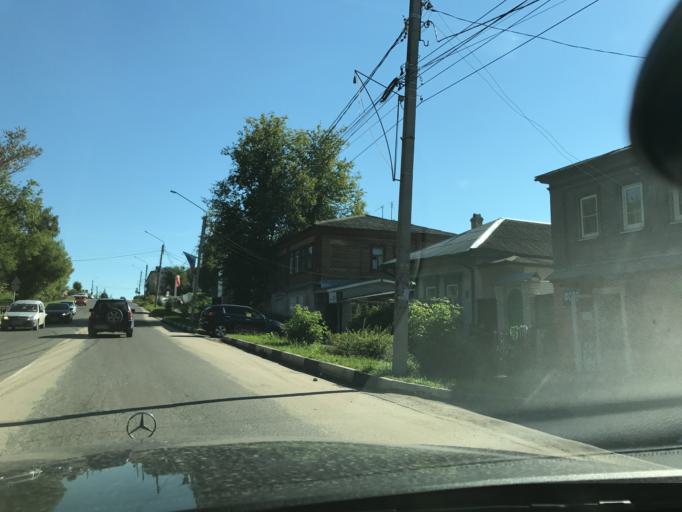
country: RU
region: Vladimir
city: Kirzhach
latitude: 56.1598
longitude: 38.8684
